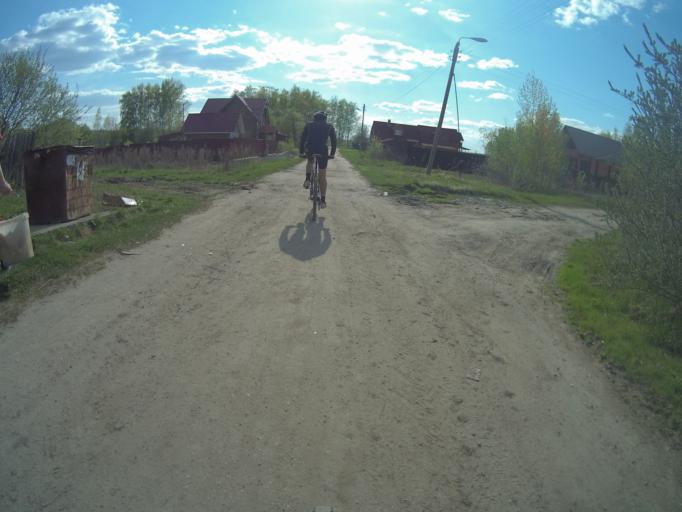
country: RU
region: Vladimir
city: Vorsha
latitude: 55.9934
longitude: 40.1953
